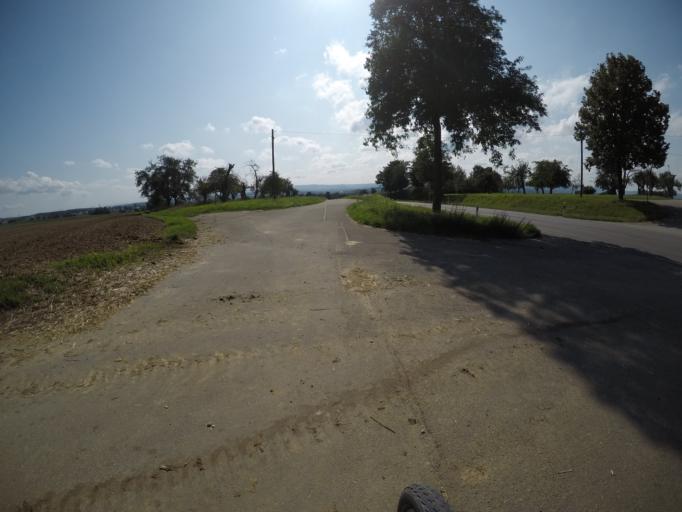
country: DE
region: Baden-Wuerttemberg
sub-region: Regierungsbezirk Stuttgart
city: Kongen
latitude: 48.6875
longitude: 9.3441
